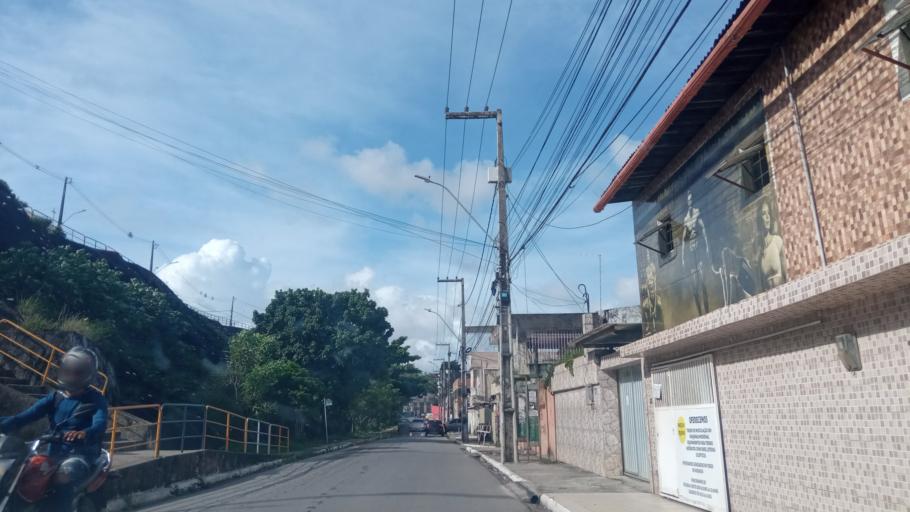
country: BR
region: Pernambuco
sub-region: Jaboatao Dos Guararapes
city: Jaboatao dos Guararapes
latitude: -8.1332
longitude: -34.9511
